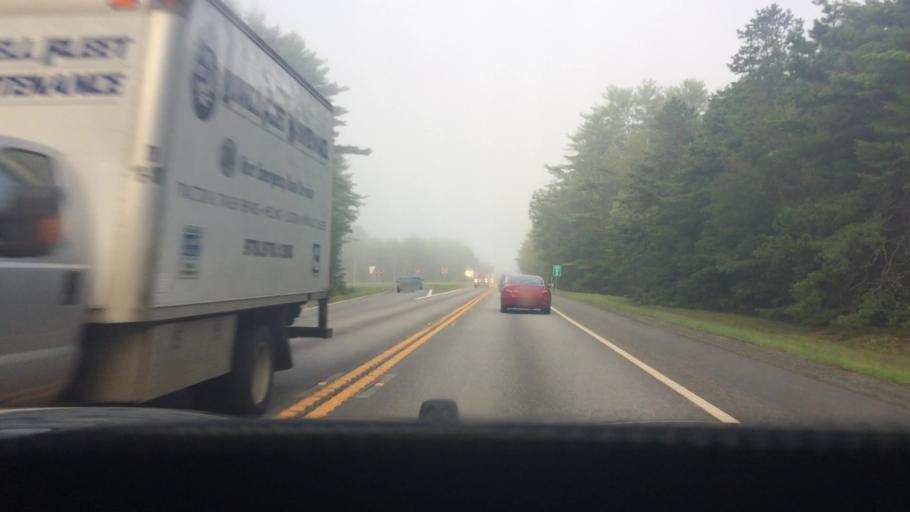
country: US
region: Massachusetts
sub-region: Franklin County
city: Orange
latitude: 42.5609
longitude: -72.2798
